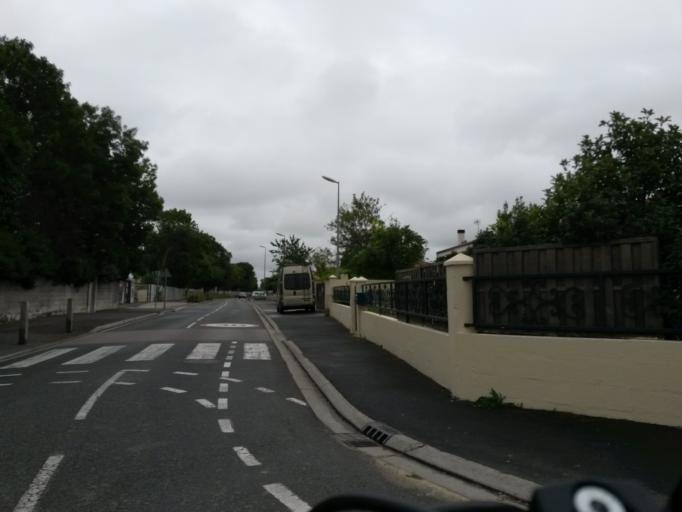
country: FR
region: Poitou-Charentes
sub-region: Departement de la Charente-Maritime
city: Saint-Xandre
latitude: 46.2054
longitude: -1.0989
